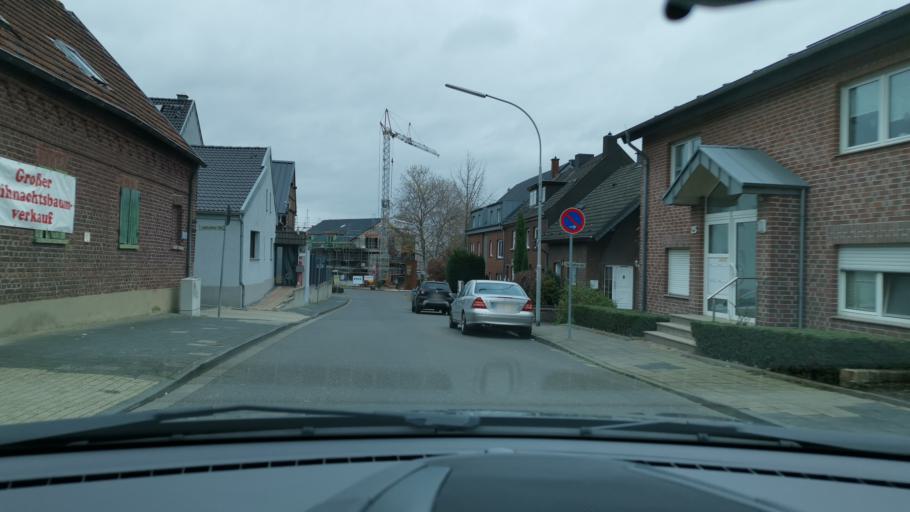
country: DE
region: North Rhine-Westphalia
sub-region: Regierungsbezirk Dusseldorf
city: Grevenbroich
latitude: 51.0706
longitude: 6.5920
